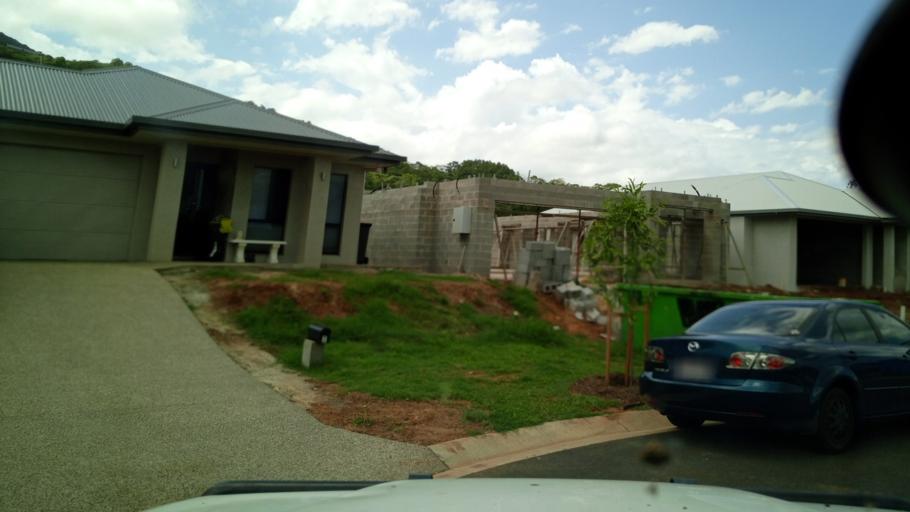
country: AU
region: Queensland
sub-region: Cairns
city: Redlynch
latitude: -16.8986
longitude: 145.6925
